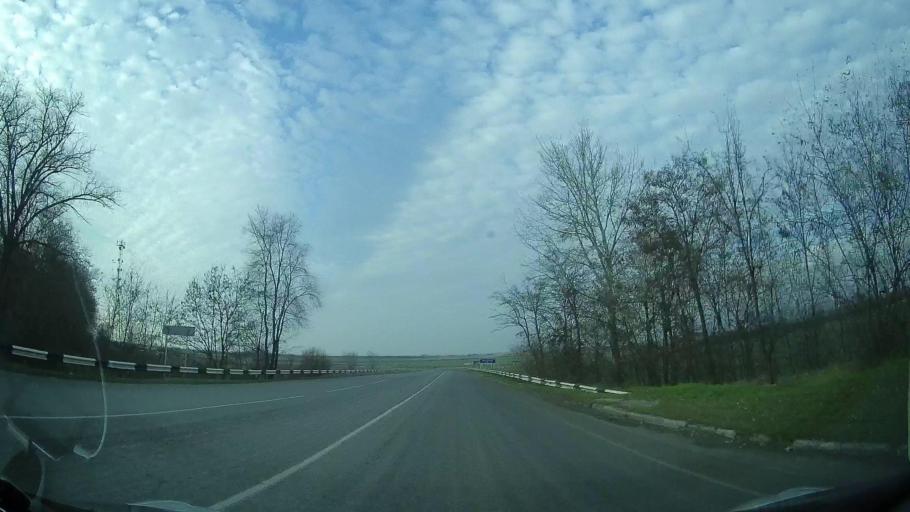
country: RU
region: Rostov
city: Bagayevskaya
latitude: 47.1639
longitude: 40.2737
